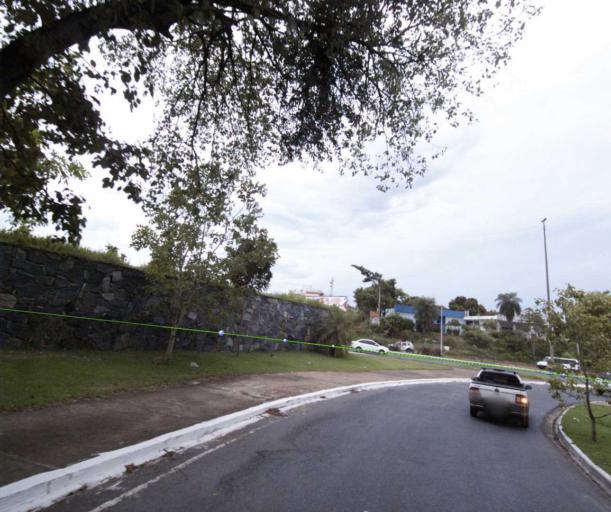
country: BR
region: Mato Grosso
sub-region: Cuiaba
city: Cuiaba
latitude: -15.6077
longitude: -56.0817
